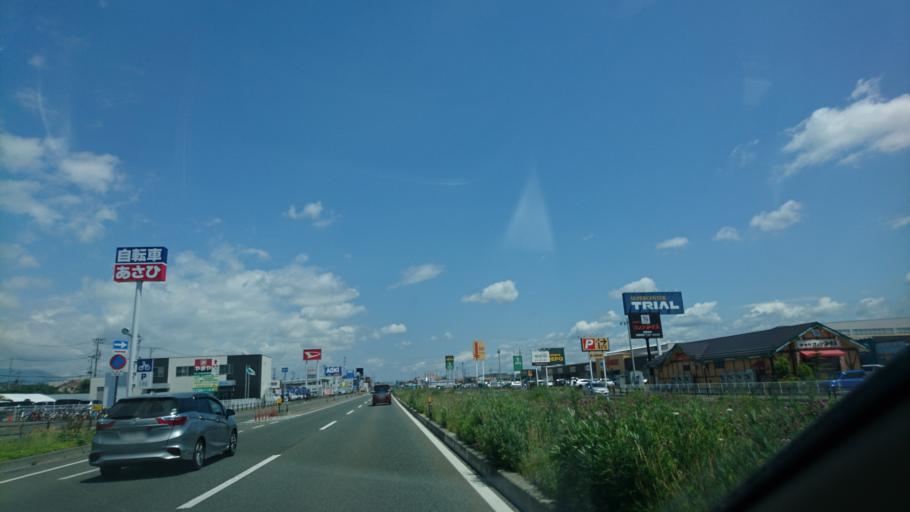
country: JP
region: Iwate
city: Morioka-shi
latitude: 39.6739
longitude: 141.1352
